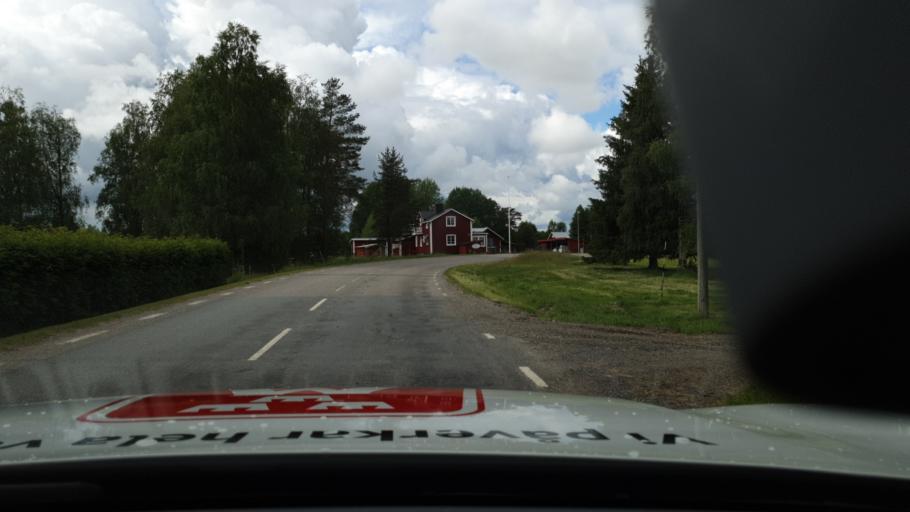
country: SE
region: Norrbotten
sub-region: Bodens Kommun
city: Saevast
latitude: 65.6061
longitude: 21.7051
